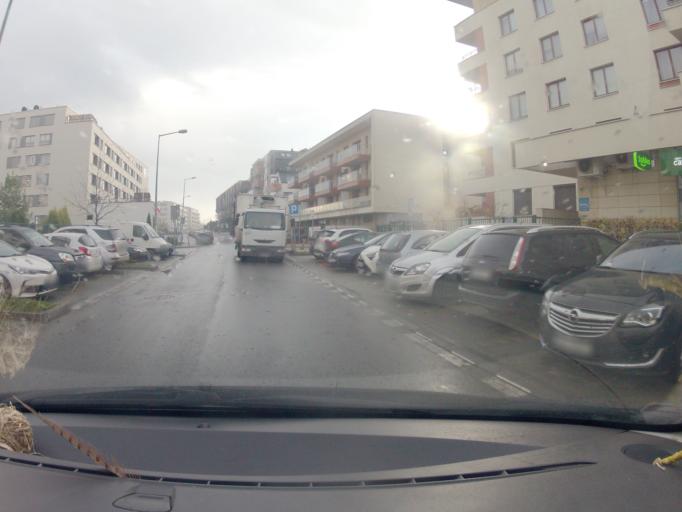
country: PL
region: Lesser Poland Voivodeship
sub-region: Krakow
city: Sidzina
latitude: 50.0143
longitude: 19.8898
